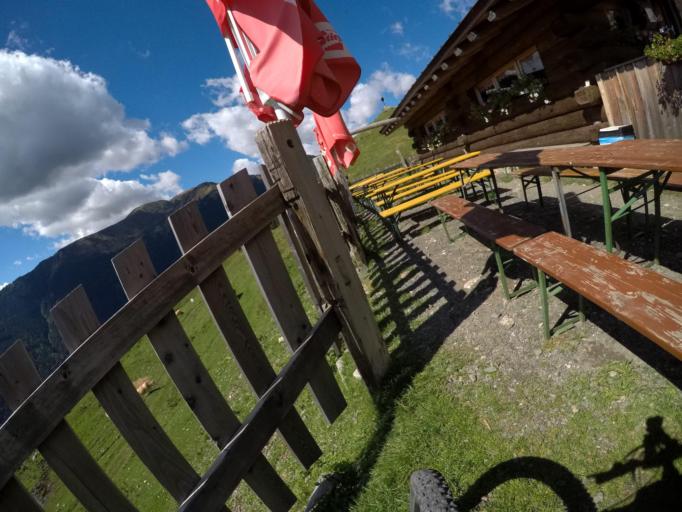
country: IT
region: Friuli Venezia Giulia
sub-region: Provincia di Udine
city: Paularo
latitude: 46.5667
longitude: 13.1214
